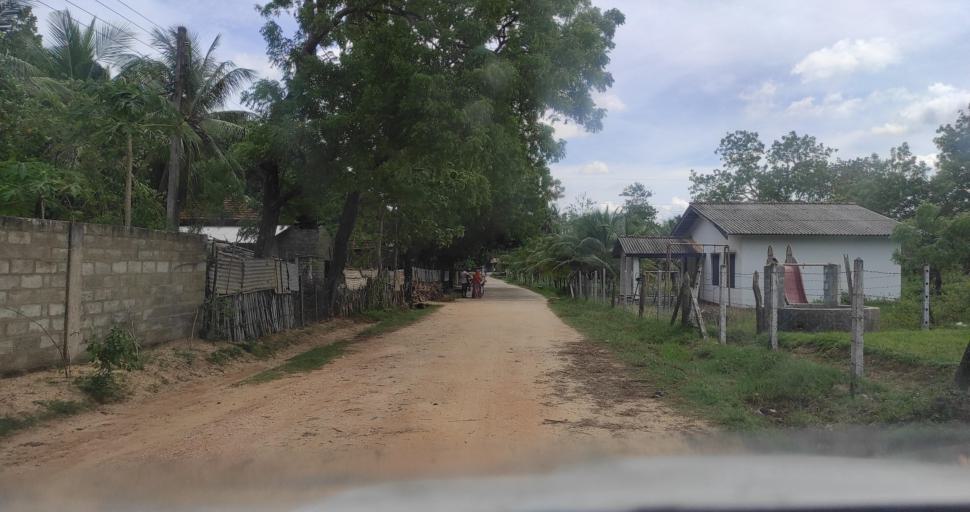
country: LK
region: Eastern Province
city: Trincomalee
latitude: 8.4406
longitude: 81.0495
